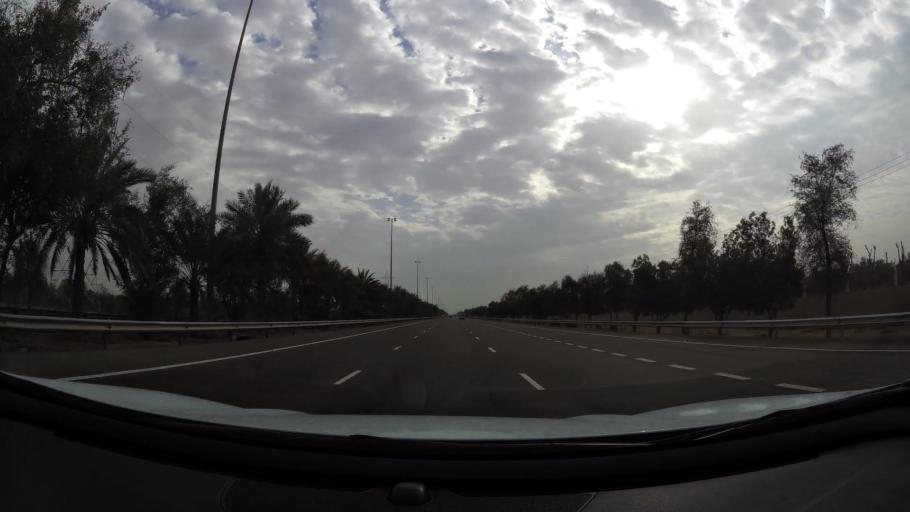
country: AE
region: Abu Dhabi
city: Al Ain
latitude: 24.2040
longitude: 55.4037
